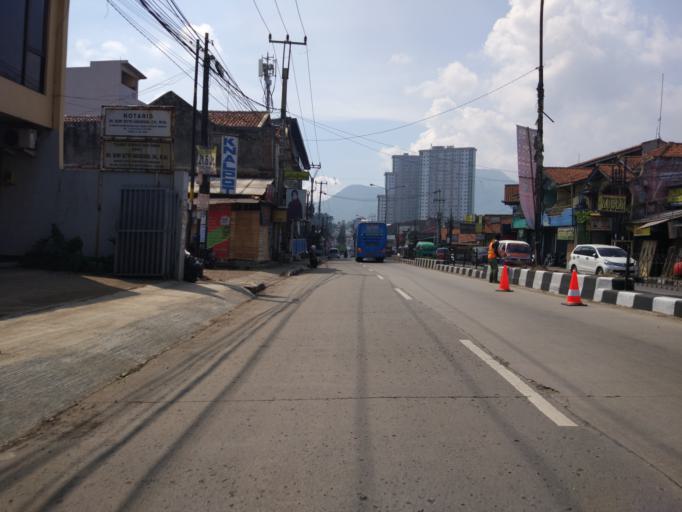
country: ID
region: West Java
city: Cileunyi
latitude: -6.9370
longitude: 107.7606
